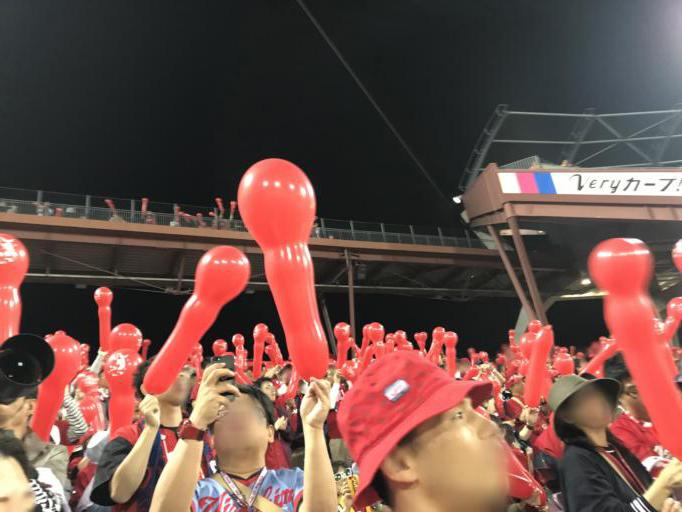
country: JP
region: Hiroshima
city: Hiroshima-shi
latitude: 34.3923
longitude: 132.4841
